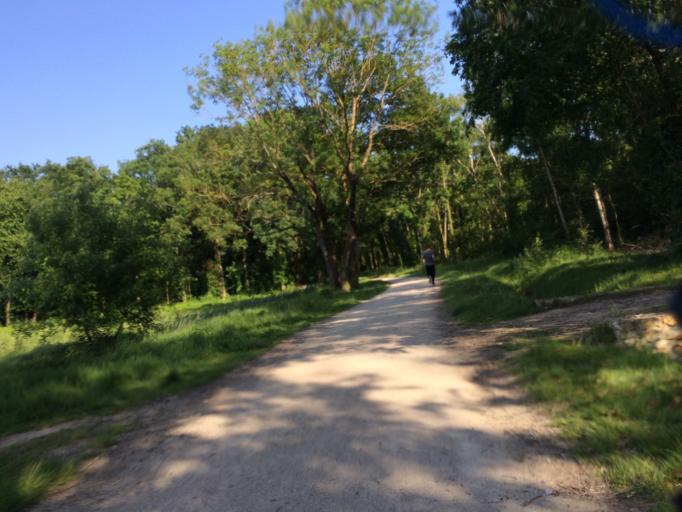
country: FR
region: Ile-de-France
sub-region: Departement de l'Essonne
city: Fleury-Merogis
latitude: 48.6275
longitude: 2.3736
